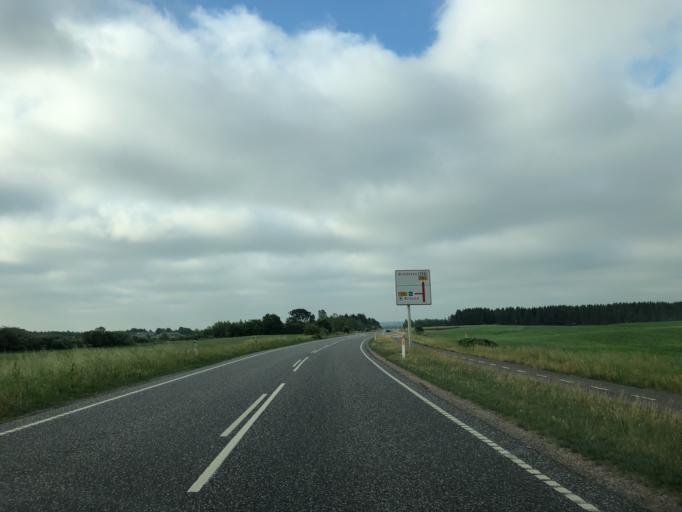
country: DK
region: South Denmark
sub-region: Vejle Kommune
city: Give
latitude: 55.8315
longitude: 9.2531
